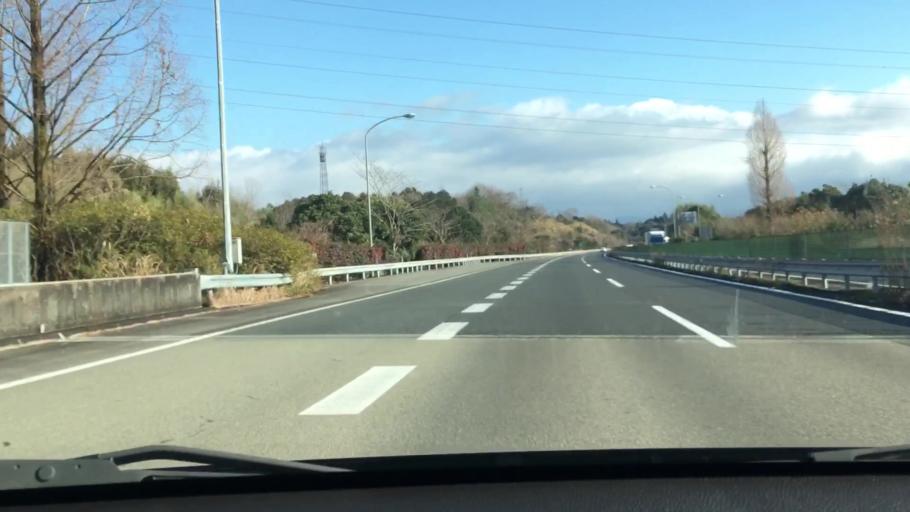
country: JP
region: Kumamoto
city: Hitoyoshi
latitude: 32.2321
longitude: 130.7707
